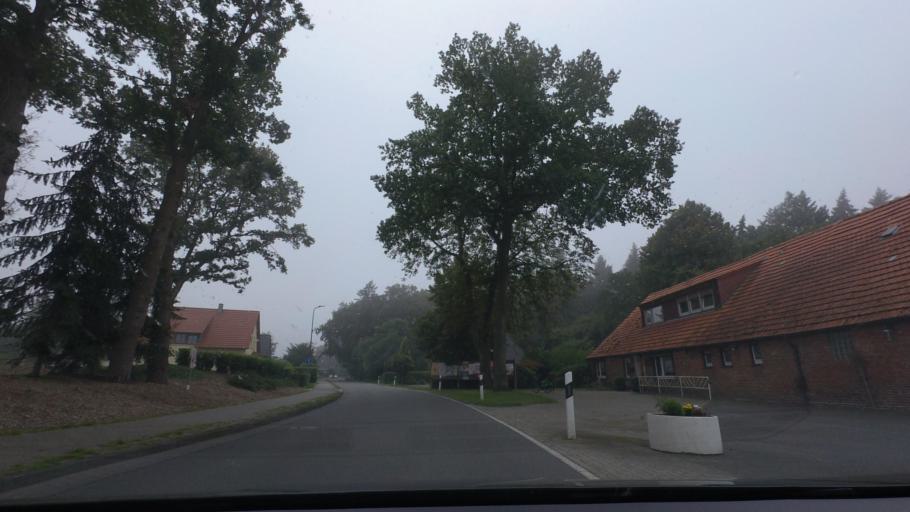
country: DE
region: Lower Saxony
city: Hude
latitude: 53.1220
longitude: 8.4523
